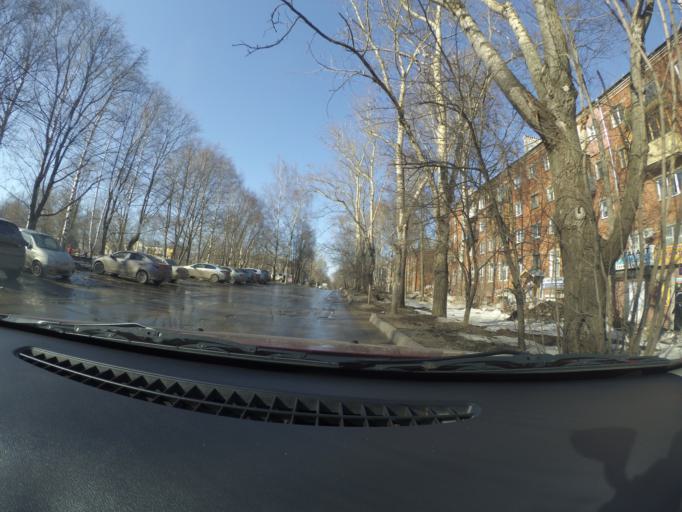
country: RU
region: Nizjnij Novgorod
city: Nizhniy Novgorod
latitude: 56.2906
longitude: 44.0043
